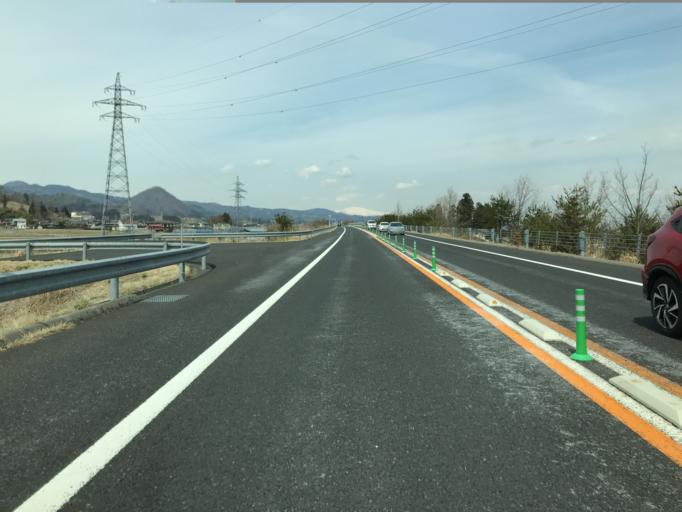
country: JP
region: Yamagata
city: Kaminoyama
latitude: 38.2115
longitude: 140.2910
